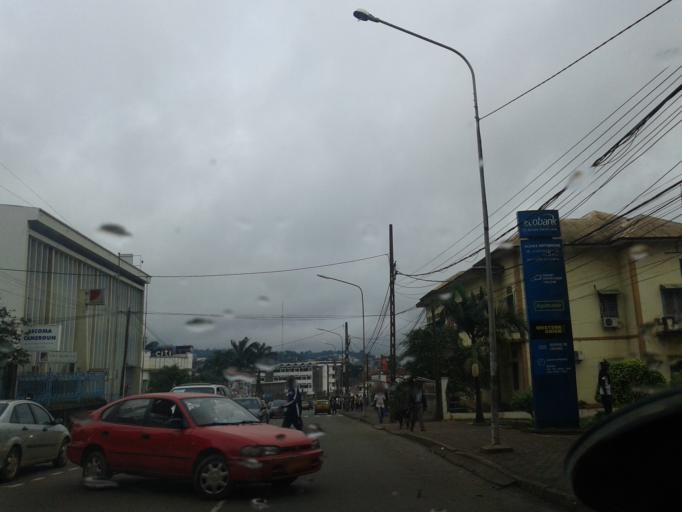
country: CM
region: Centre
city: Yaounde
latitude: 3.8771
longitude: 11.5166
